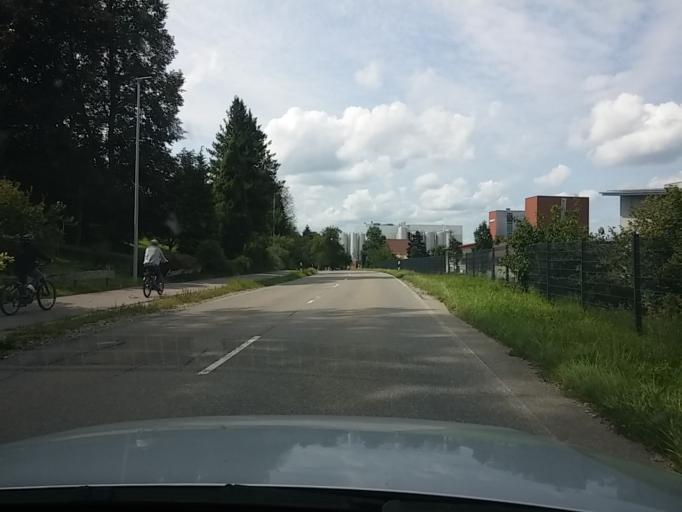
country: DE
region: Baden-Wuerttemberg
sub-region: Tuebingen Region
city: Leutkirch im Allgau
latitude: 47.8201
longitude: 10.0553
